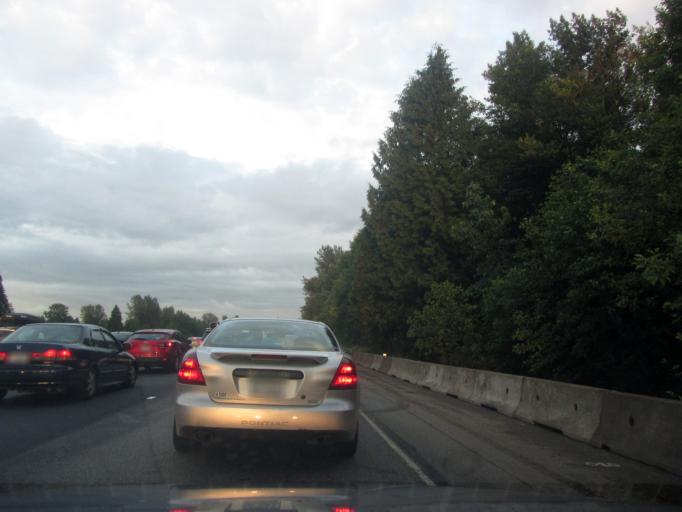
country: CA
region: British Columbia
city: Langley
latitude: 49.1139
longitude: -122.5249
